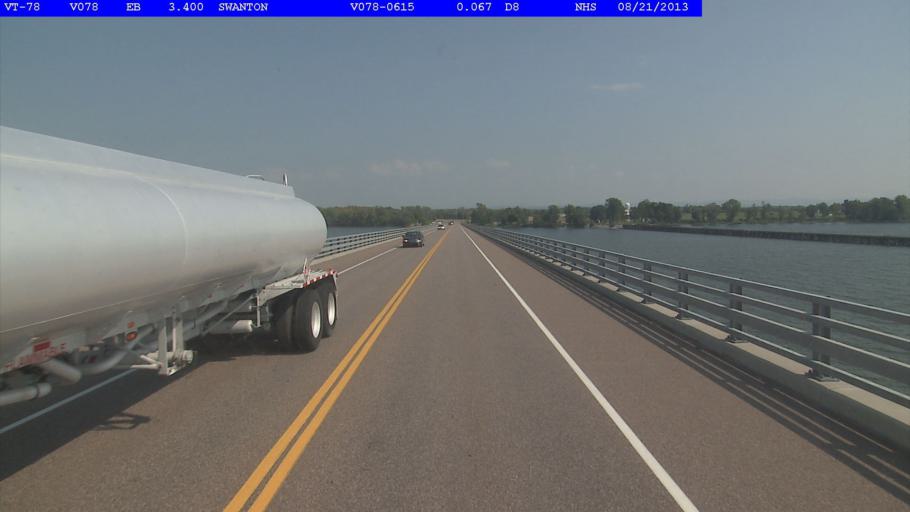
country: US
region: Vermont
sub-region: Franklin County
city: Swanton
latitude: 44.9726
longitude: -73.2191
